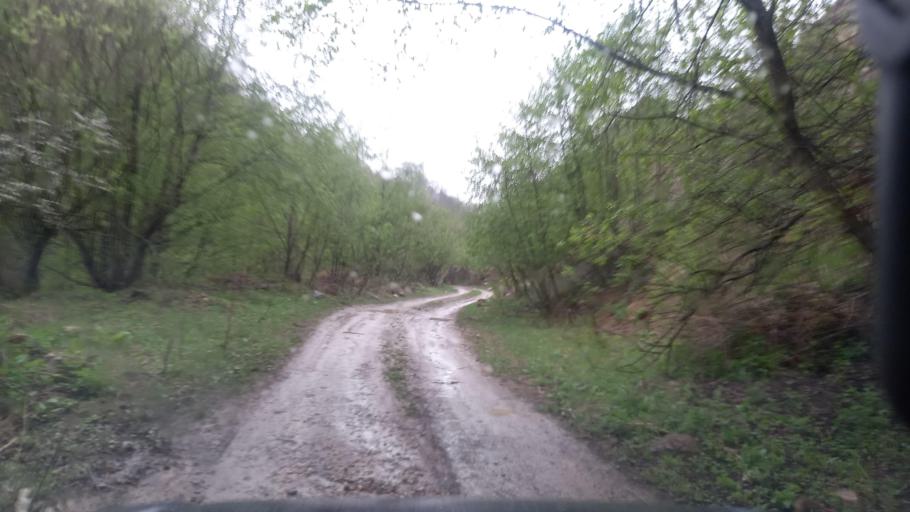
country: RU
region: Kabardino-Balkariya
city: Bylym
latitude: 43.5999
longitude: 42.9376
